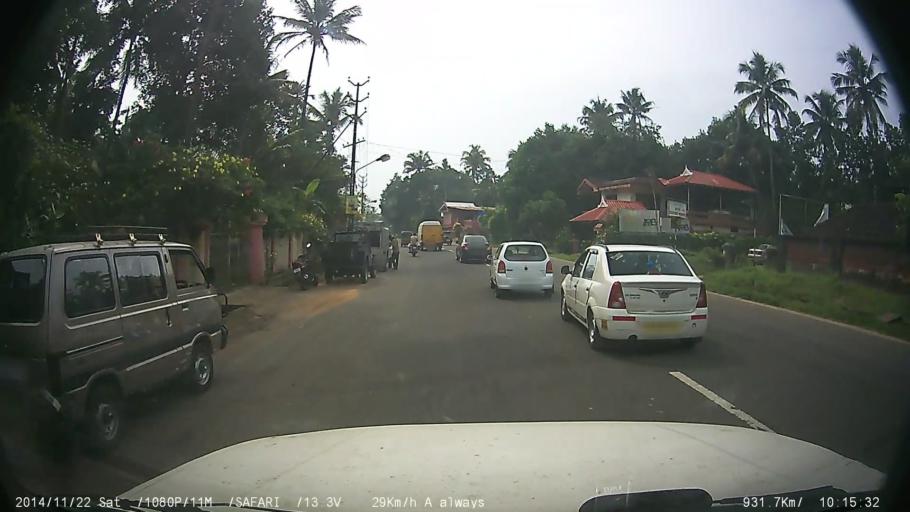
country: IN
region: Kerala
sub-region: Ernakulam
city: Muvattupula
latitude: 10.0004
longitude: 76.5715
